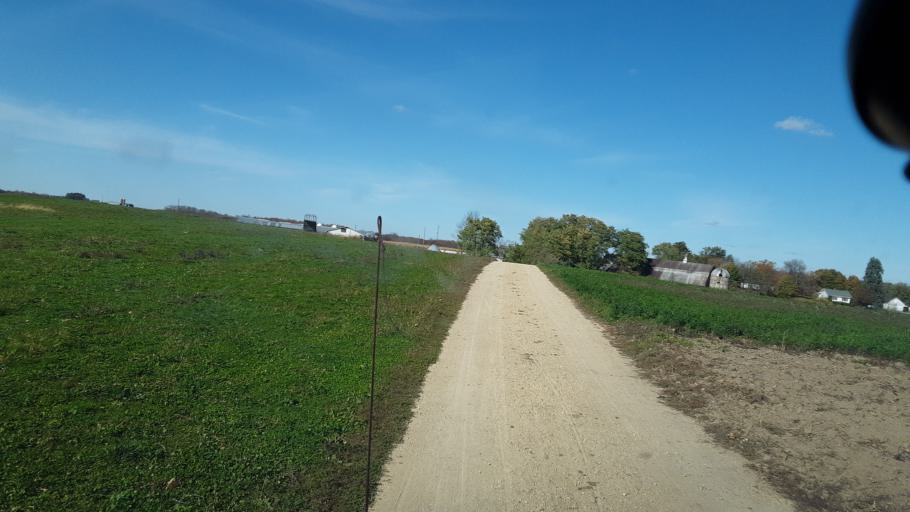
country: US
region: Wisconsin
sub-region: Vernon County
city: Hillsboro
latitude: 43.6841
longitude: -90.4095
